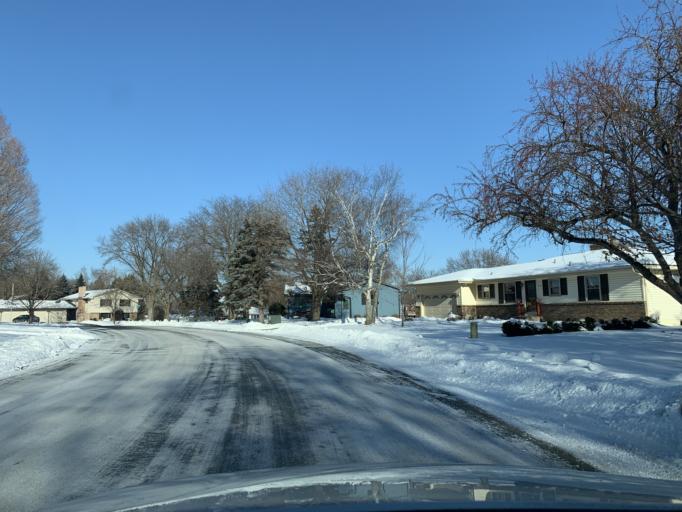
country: US
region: Minnesota
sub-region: Scott County
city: Savage
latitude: 44.8232
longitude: -93.3405
